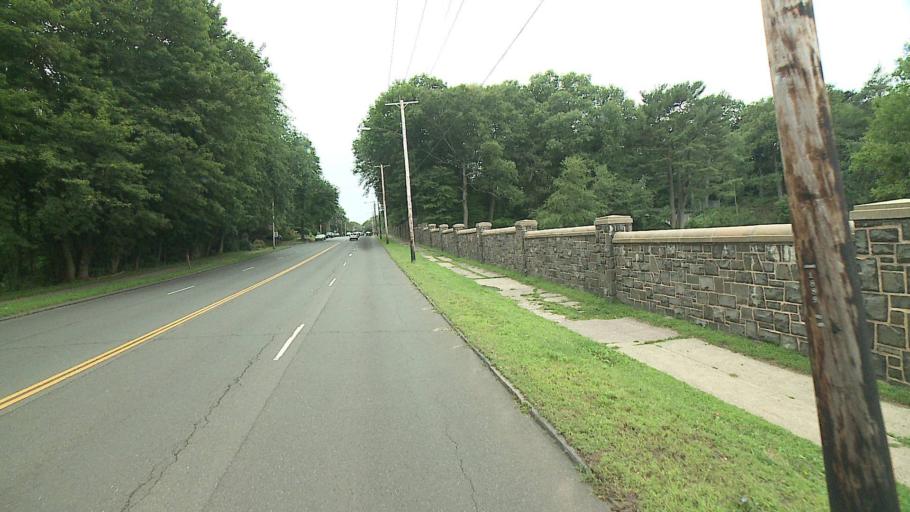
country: US
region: Connecticut
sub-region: New Haven County
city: New Haven
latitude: 41.3346
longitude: -72.9119
